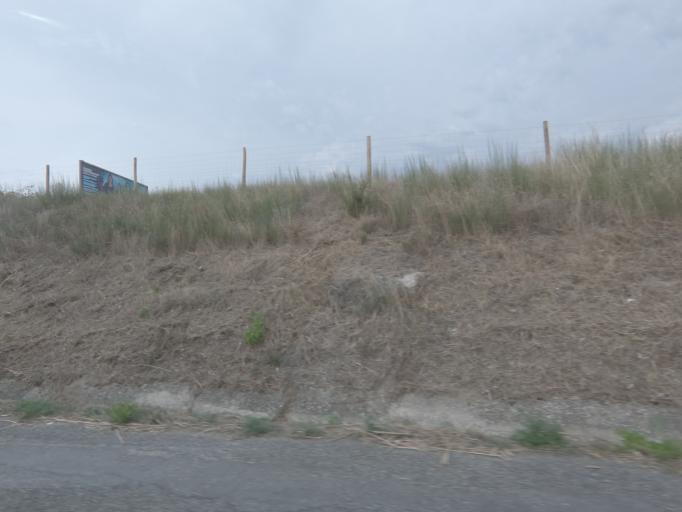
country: PT
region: Viseu
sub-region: Concelho de Tondela
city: Tondela
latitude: 40.5148
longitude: -8.0919
